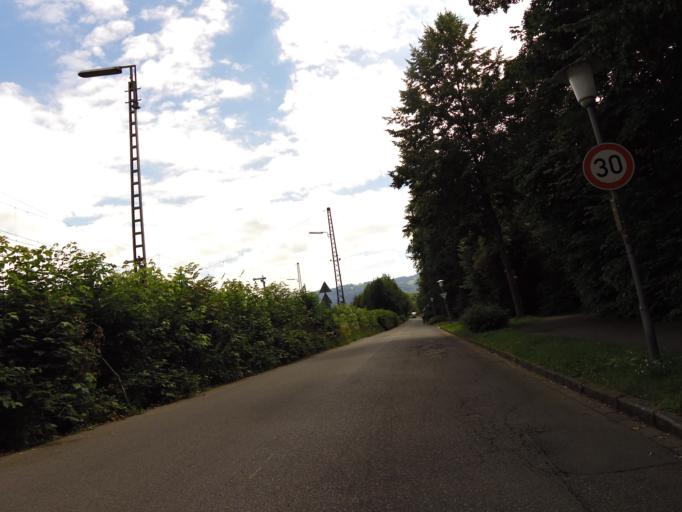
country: DE
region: Bavaria
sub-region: Swabia
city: Lindau
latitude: 47.5519
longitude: 9.6970
